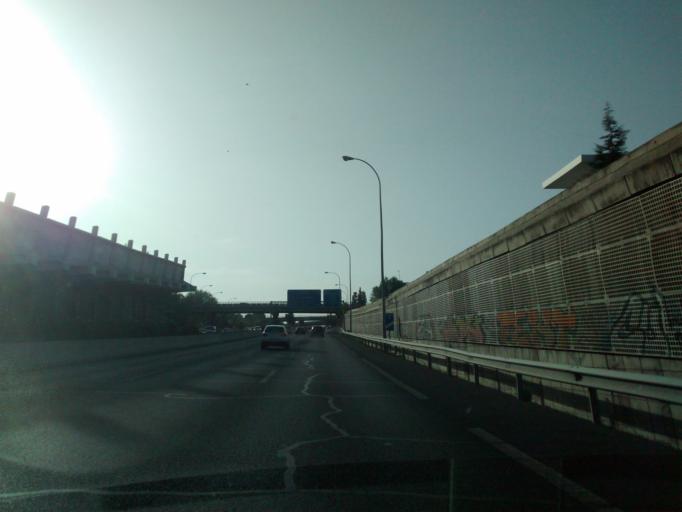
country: ES
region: Madrid
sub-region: Provincia de Madrid
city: Hortaleza
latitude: 40.4757
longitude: -3.6364
